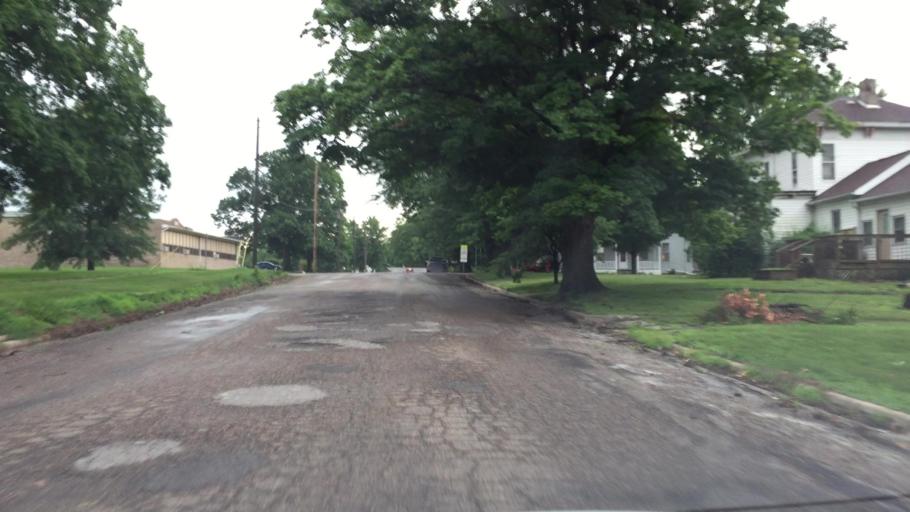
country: US
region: Illinois
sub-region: Hancock County
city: Warsaw
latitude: 40.3562
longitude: -91.4289
